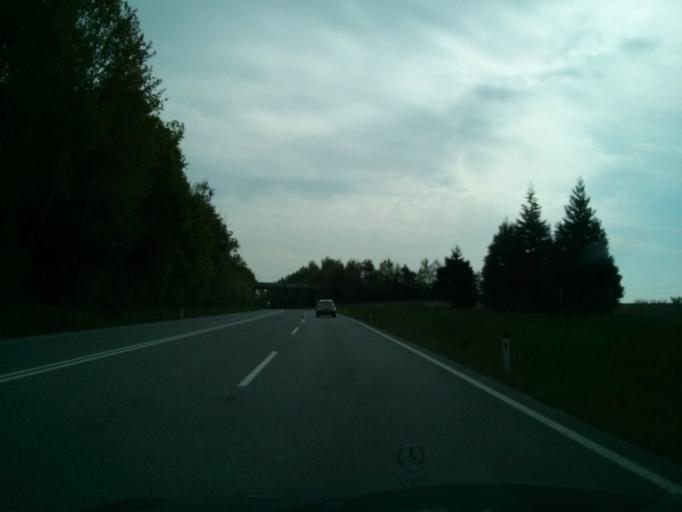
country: AT
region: Burgenland
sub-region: Politischer Bezirk Oberwart
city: Markt Allhau
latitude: 47.2767
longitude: 16.1081
